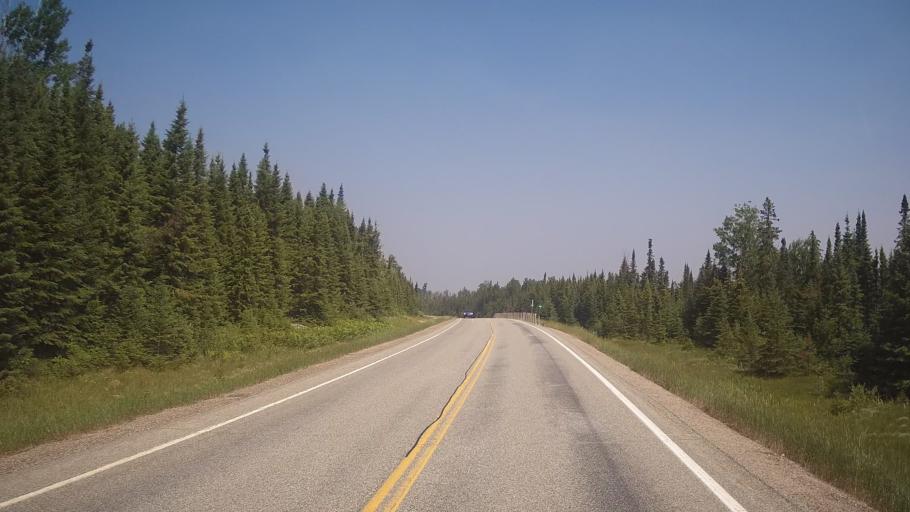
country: CA
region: Ontario
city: Timmins
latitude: 48.1719
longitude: -81.5823
